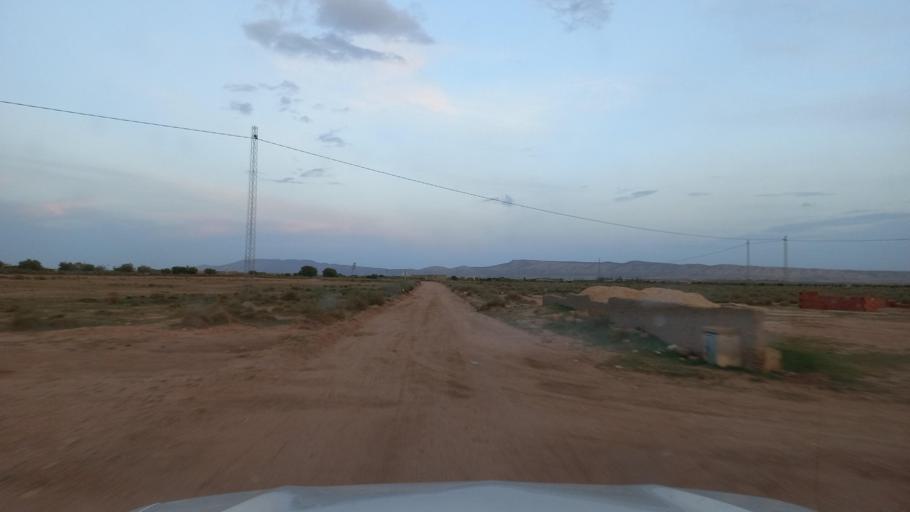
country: TN
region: Al Qasrayn
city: Sbiba
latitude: 35.3495
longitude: 9.0393
